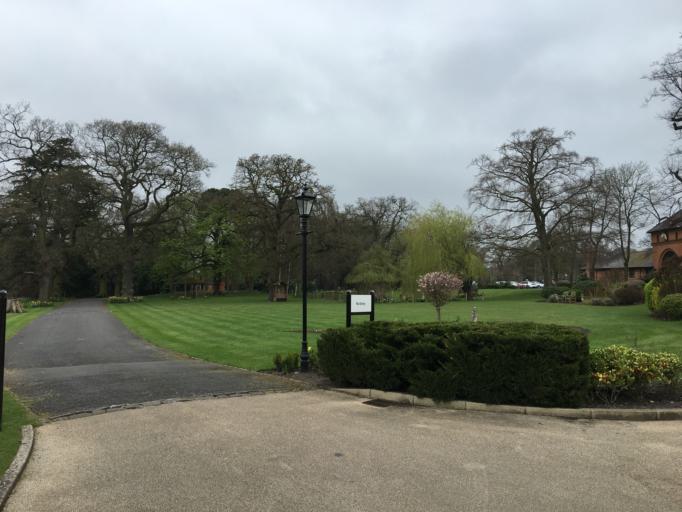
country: GB
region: England
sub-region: Cheshire East
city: Nantwich
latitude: 53.0988
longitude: -2.5098
